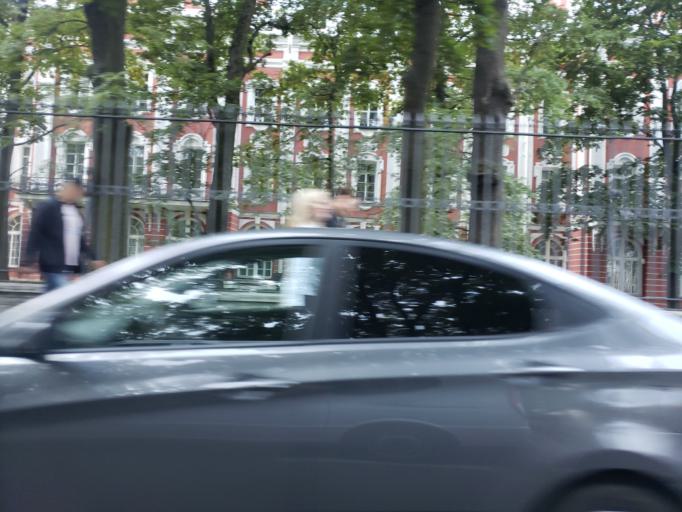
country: RU
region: St.-Petersburg
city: Saint Petersburg
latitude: 59.9427
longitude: 30.2989
